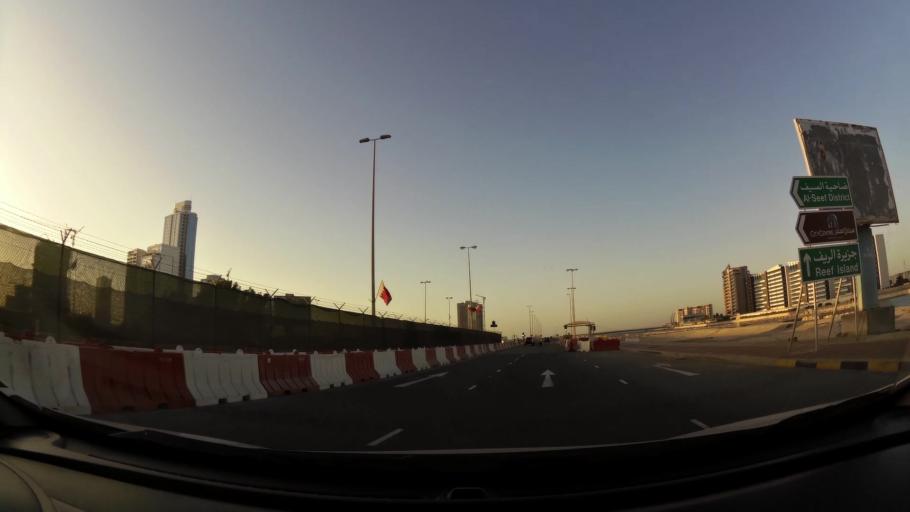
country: BH
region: Manama
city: Jidd Hafs
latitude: 26.2342
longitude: 50.5607
